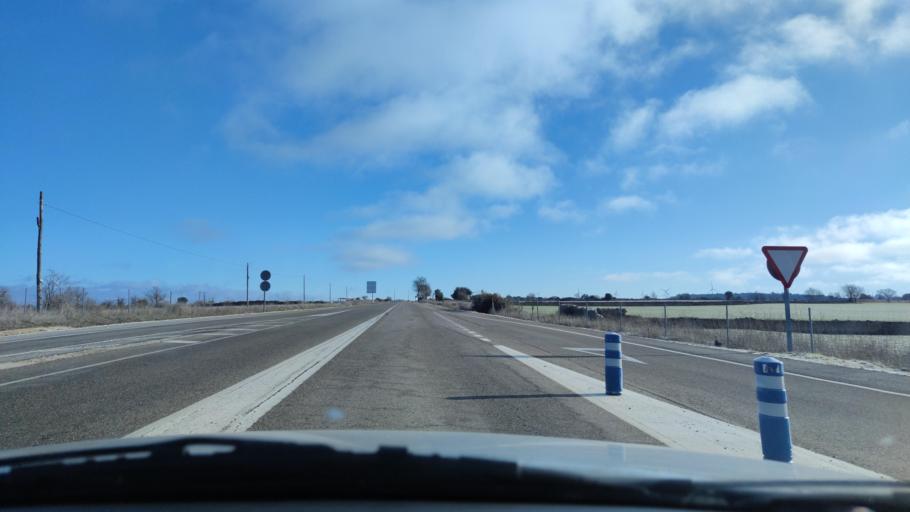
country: ES
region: Catalonia
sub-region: Provincia de Barcelona
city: Pujalt
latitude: 41.7288
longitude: 1.3839
